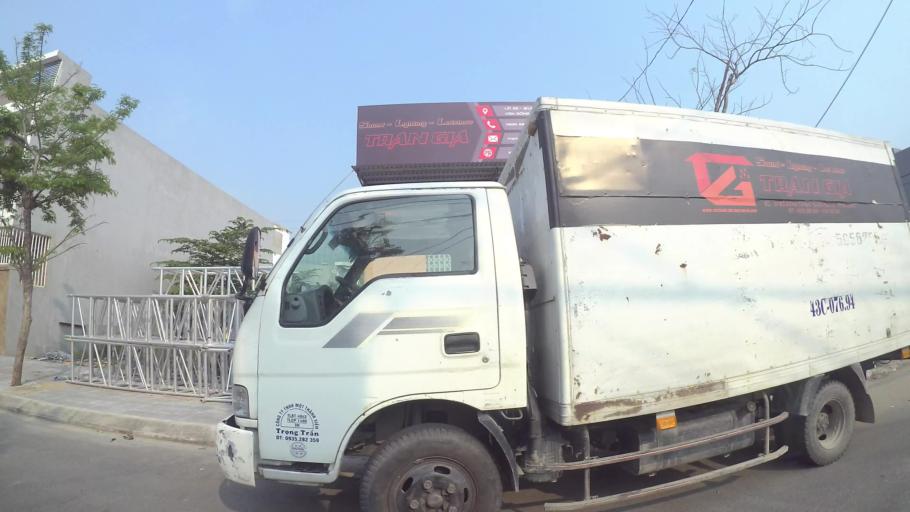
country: VN
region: Da Nang
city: Cam Le
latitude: 16.0101
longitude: 108.2242
